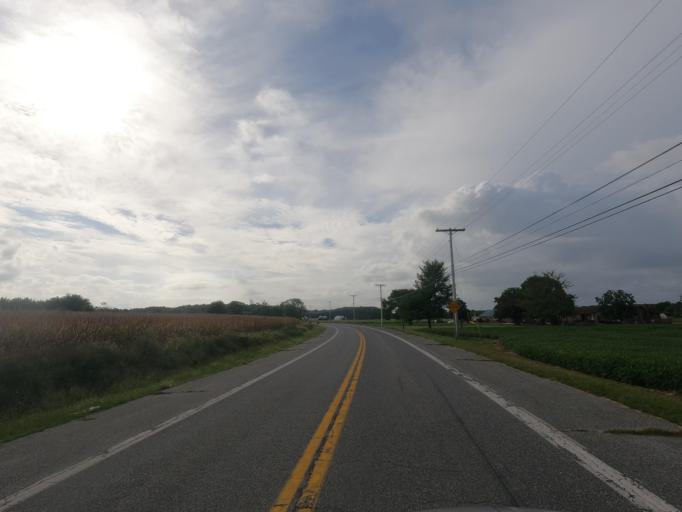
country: US
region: Virginia
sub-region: Northumberland County
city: Heathsville
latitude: 38.0817
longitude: -76.3579
